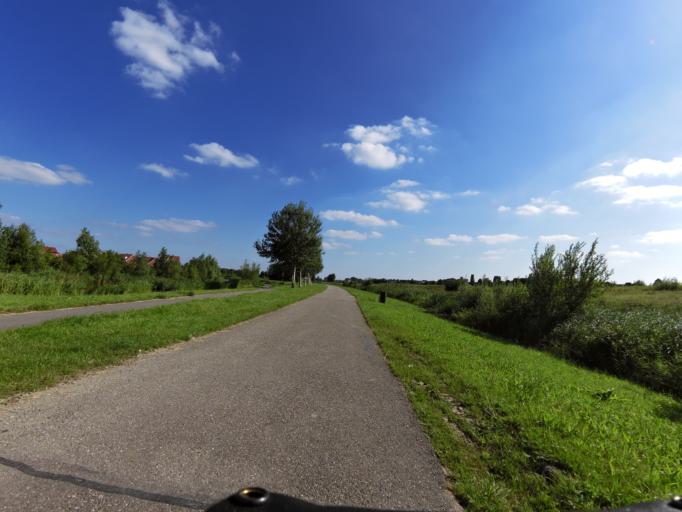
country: NL
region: South Holland
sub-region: Gemeente Binnenmaas
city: Heinenoord
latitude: 51.8589
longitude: 4.4613
